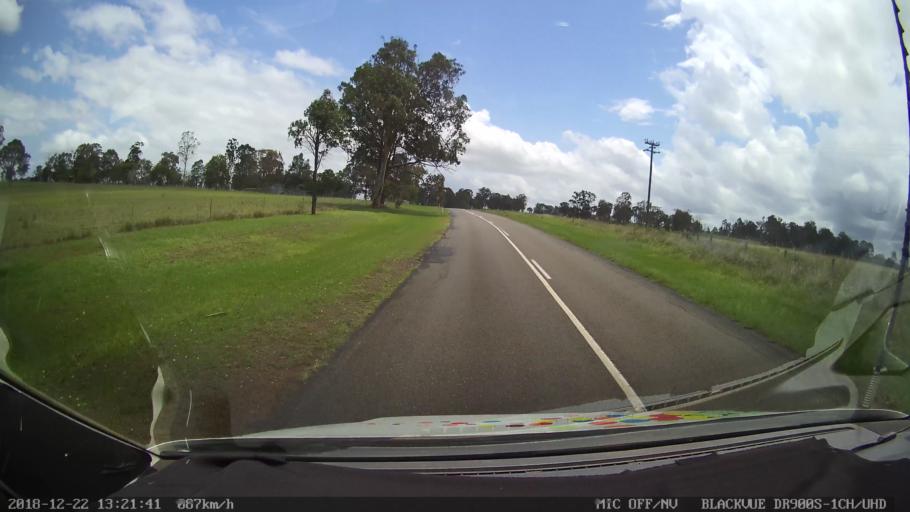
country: AU
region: New South Wales
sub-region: Clarence Valley
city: Coutts Crossing
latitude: -29.7793
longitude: 152.9180
